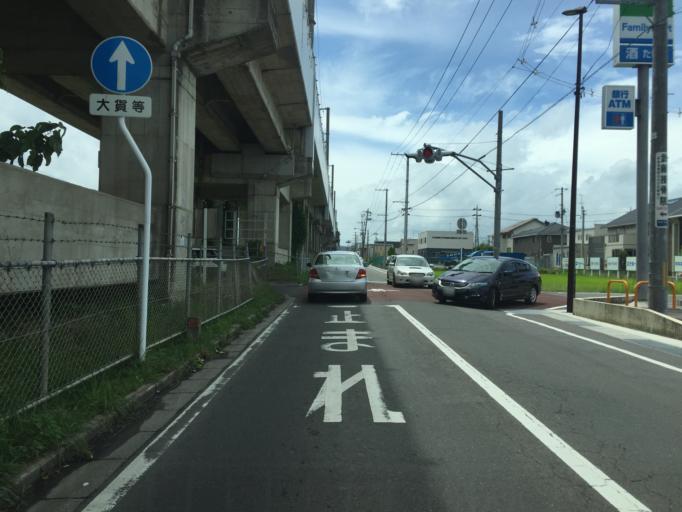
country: JP
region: Fukushima
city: Fukushima-shi
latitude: 37.7354
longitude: 140.4579
